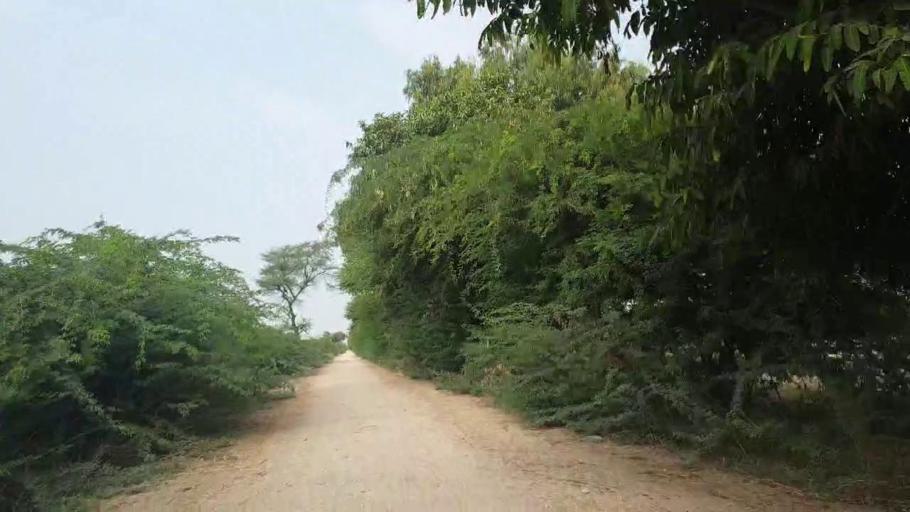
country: PK
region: Sindh
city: Badin
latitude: 24.5972
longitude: 68.7412
